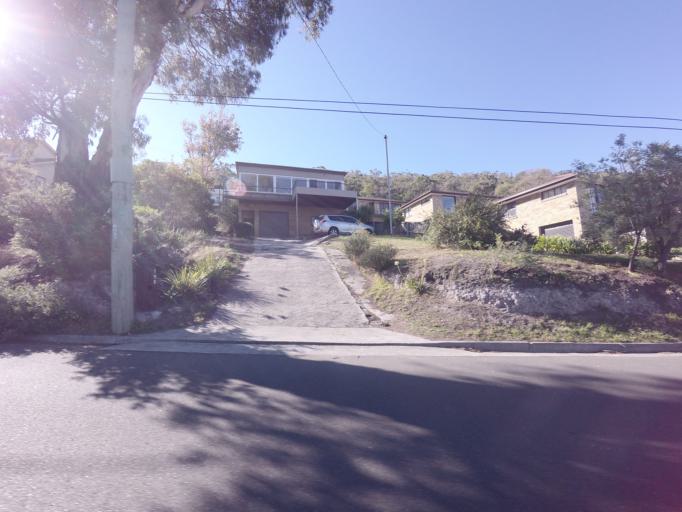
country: AU
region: Tasmania
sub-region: Clarence
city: Lindisfarne
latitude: -42.8463
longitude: 147.3418
